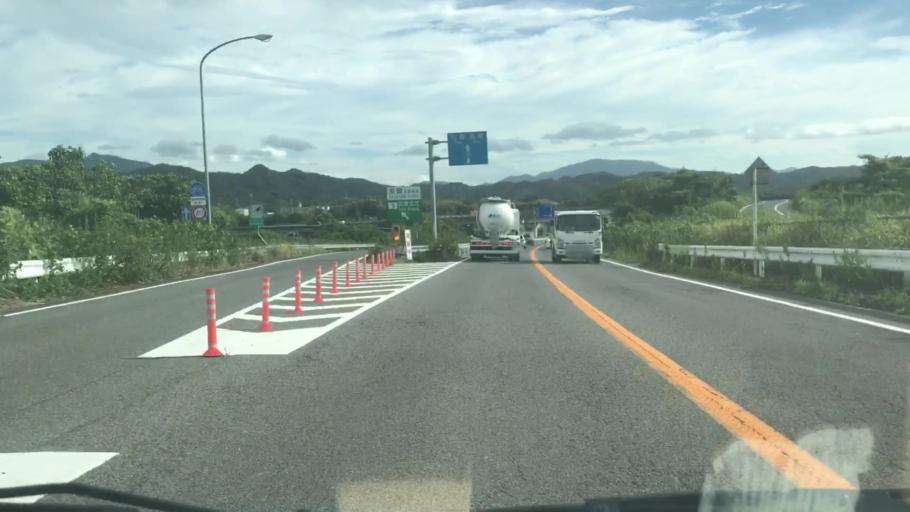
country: JP
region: Saga Prefecture
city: Takeocho-takeo
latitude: 33.2120
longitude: 130.0499
